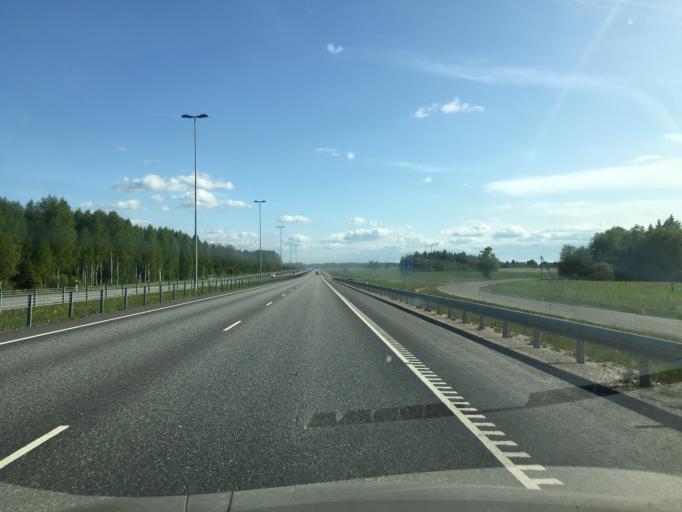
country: EE
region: Harju
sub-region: Rae vald
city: Vaida
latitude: 59.2172
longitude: 25.0357
